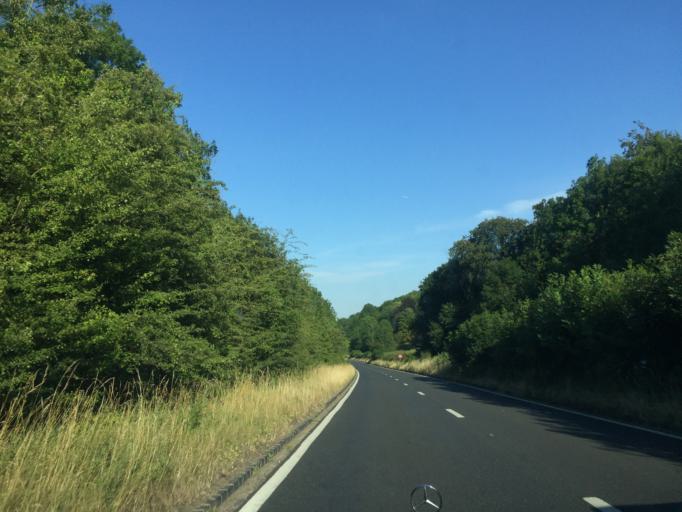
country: GB
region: England
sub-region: Oxfordshire
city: Rotherfield Peppard
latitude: 51.5571
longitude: -0.9429
